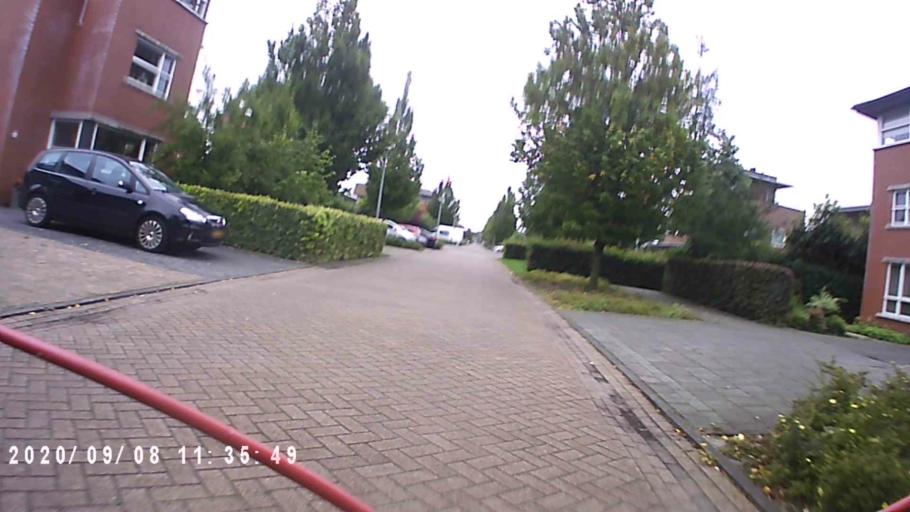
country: NL
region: Groningen
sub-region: Gemeente Hoogezand-Sappemeer
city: Sappemeer
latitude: 53.1581
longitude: 6.7807
